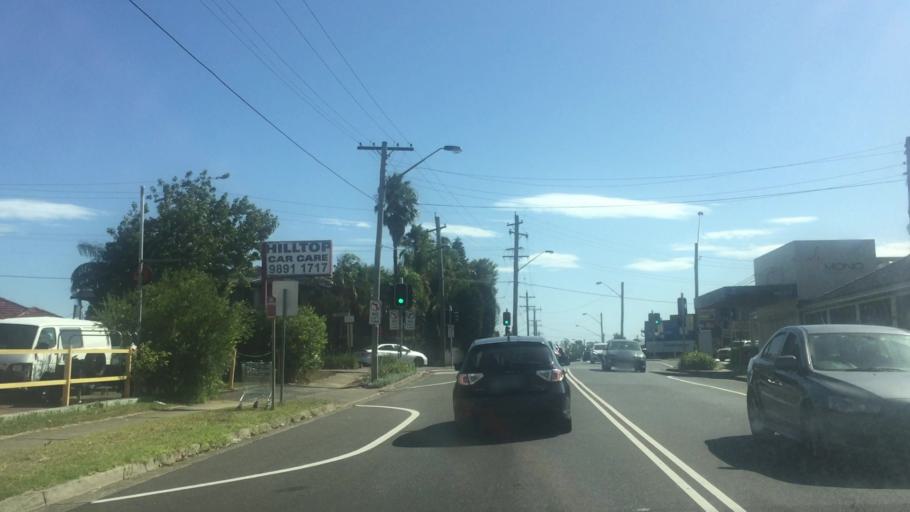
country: AU
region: New South Wales
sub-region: Holroyd
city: Merrylands
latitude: -33.8263
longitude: 150.9836
